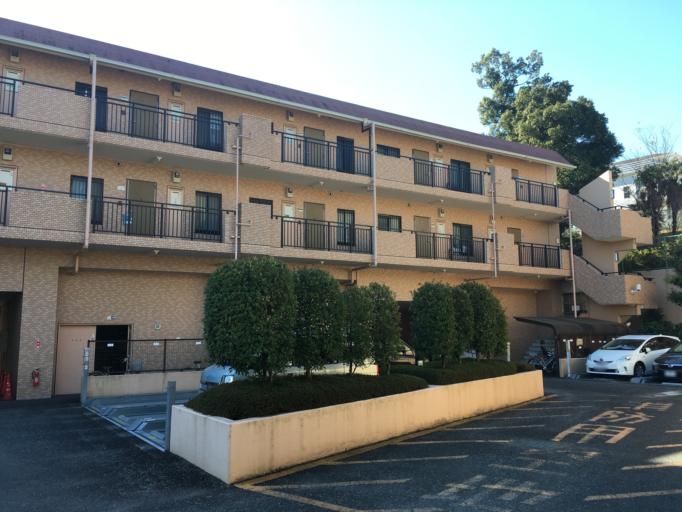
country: JP
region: Kanagawa
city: Minami-rinkan
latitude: 35.4623
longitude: 139.4708
